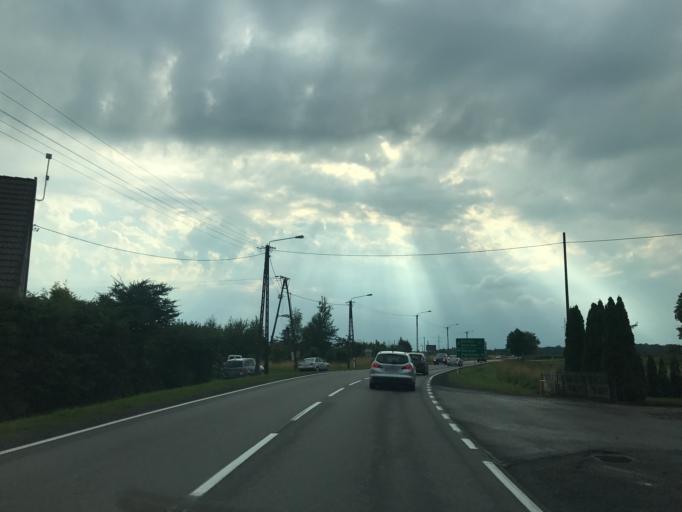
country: PL
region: Pomeranian Voivodeship
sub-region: Powiat czluchowski
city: Czluchow
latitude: 53.6866
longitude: 17.3251
